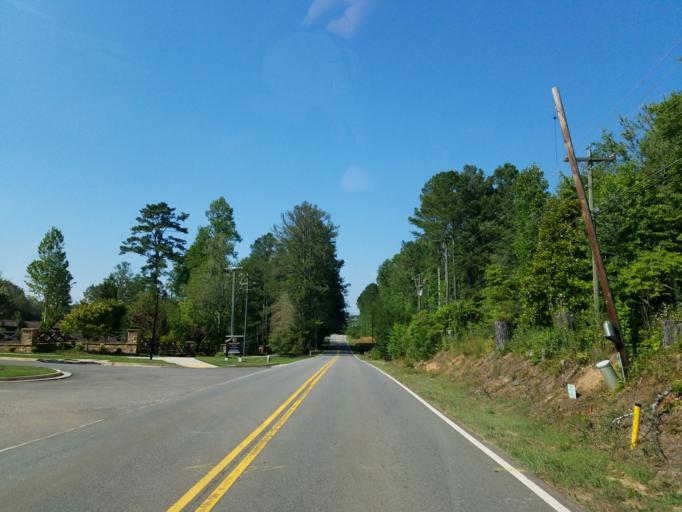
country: US
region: Georgia
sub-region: Fulton County
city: Milton
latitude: 34.1757
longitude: -84.3266
